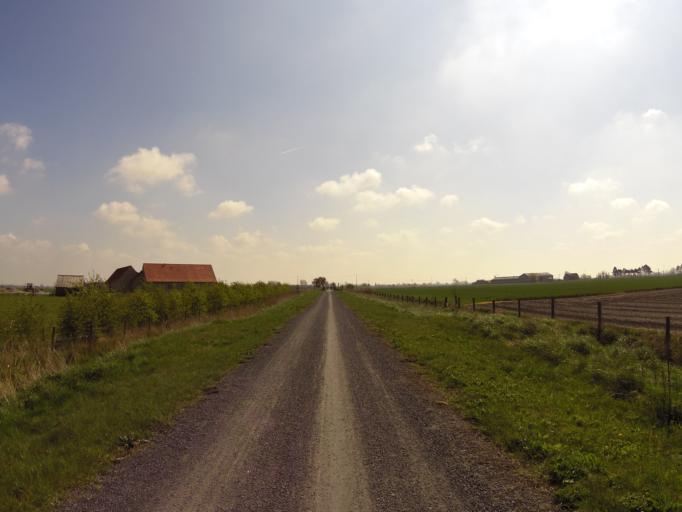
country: BE
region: Flanders
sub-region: Provincie West-Vlaanderen
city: Nieuwpoort
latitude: 51.1044
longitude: 2.7730
